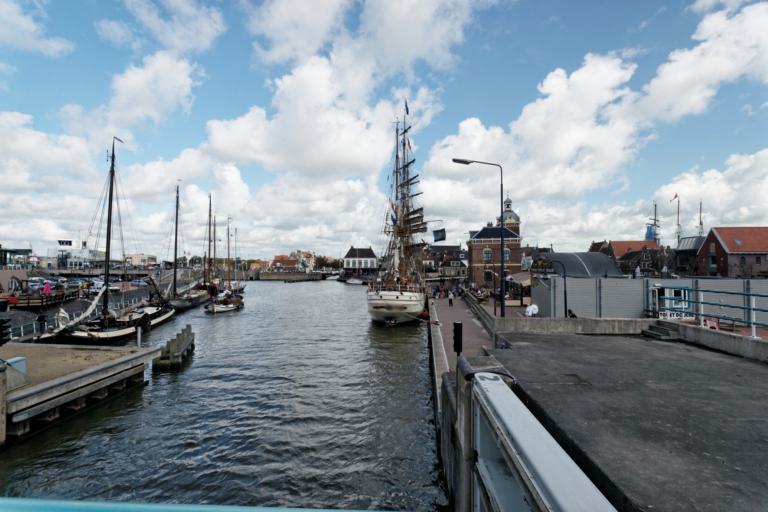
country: NL
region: Friesland
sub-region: Gemeente Harlingen
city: Harlingen
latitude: 53.1754
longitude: 5.4116
